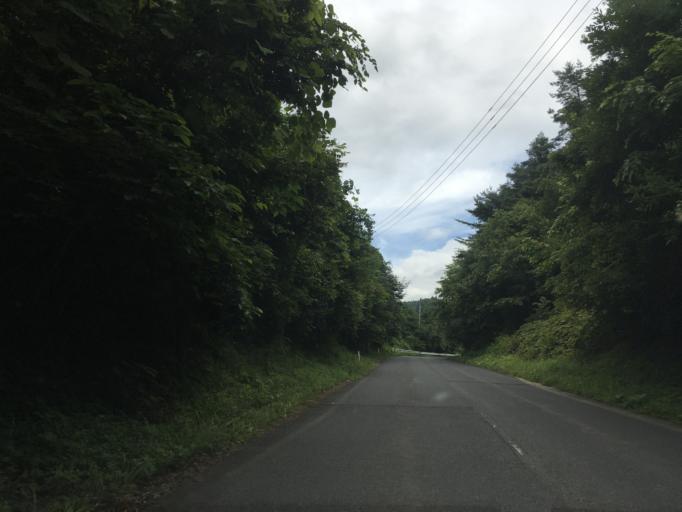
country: JP
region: Iwate
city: Ichinoseki
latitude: 38.8699
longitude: 141.3946
